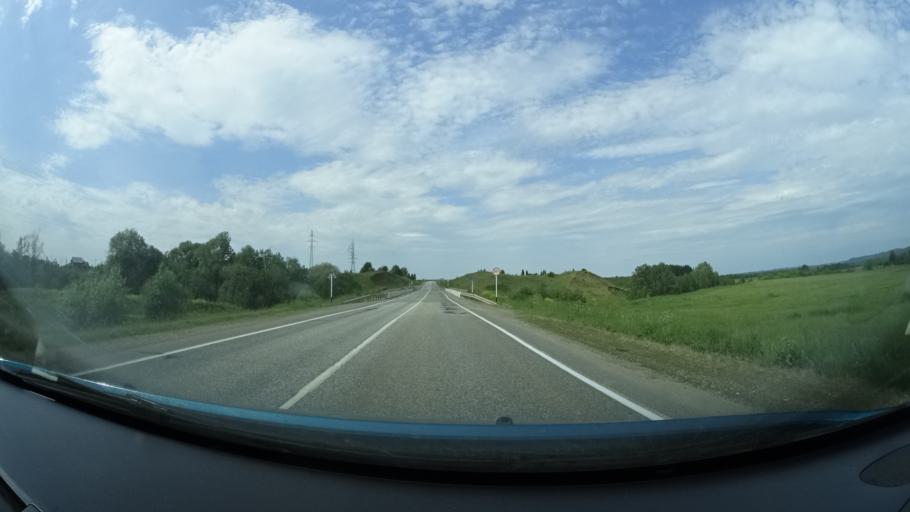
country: RU
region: Perm
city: Barda
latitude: 57.0904
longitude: 55.5372
